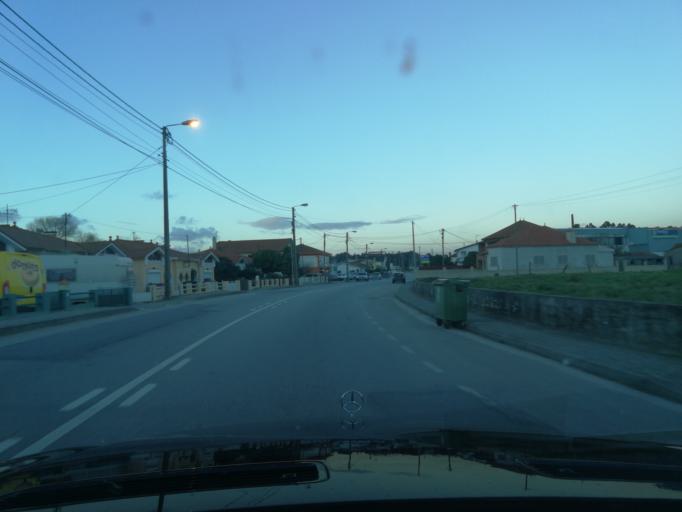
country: PT
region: Aveiro
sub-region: Estarreja
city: Estarreja
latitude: 40.7664
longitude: -8.5715
